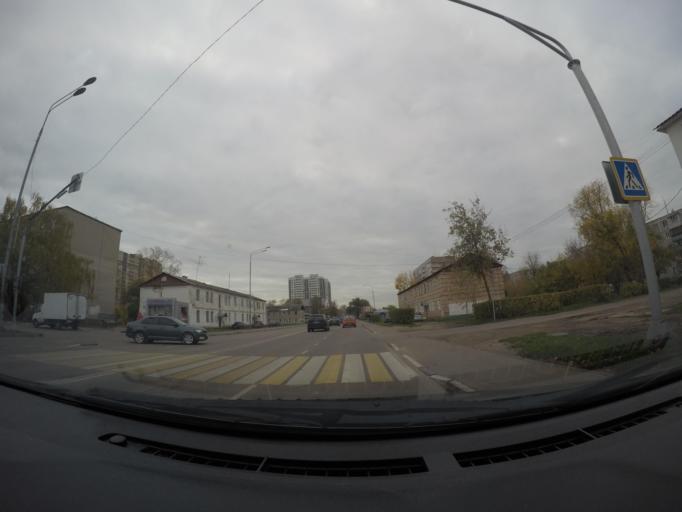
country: RU
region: Moskovskaya
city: Staraya Kupavna
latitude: 55.8050
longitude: 38.1800
